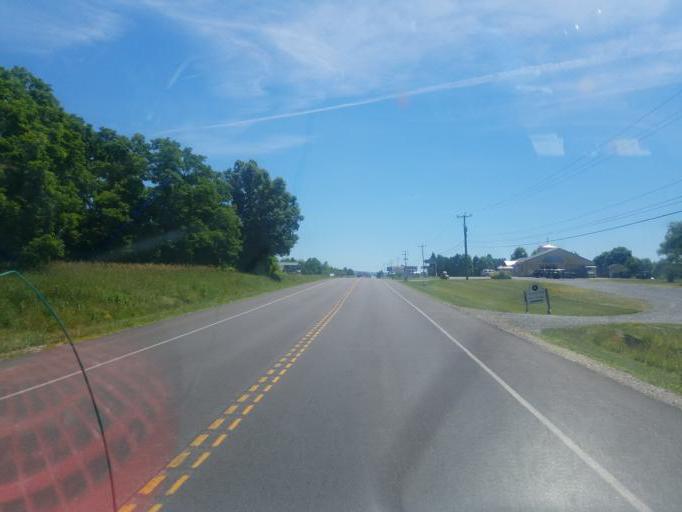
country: US
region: New York
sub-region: Yates County
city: Dundee
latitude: 42.5918
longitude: -76.9418
